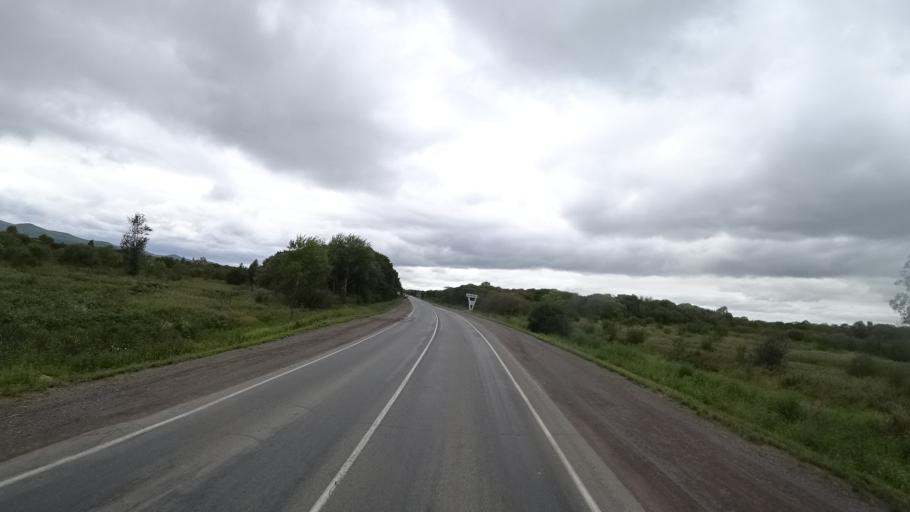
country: RU
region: Primorskiy
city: Chernigovka
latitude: 44.3449
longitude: 132.5989
